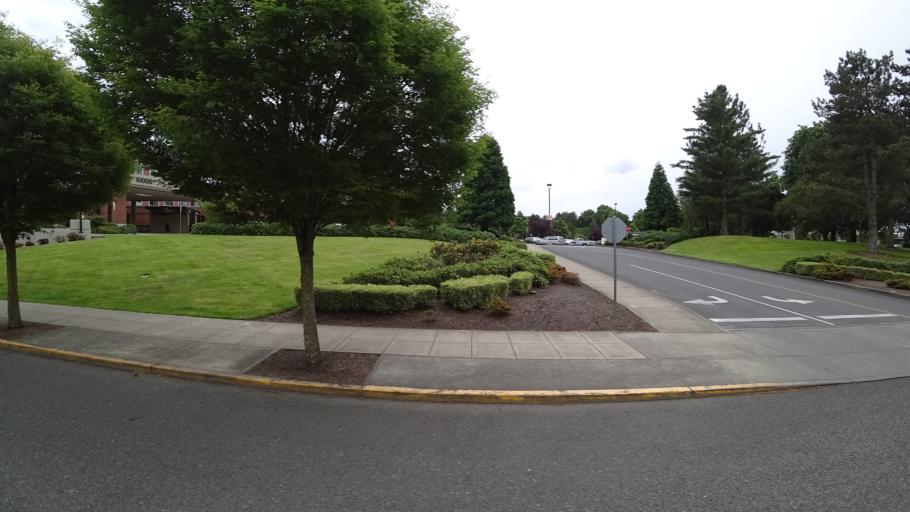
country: US
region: Oregon
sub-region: Multnomah County
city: Lents
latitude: 45.5140
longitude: -122.5600
